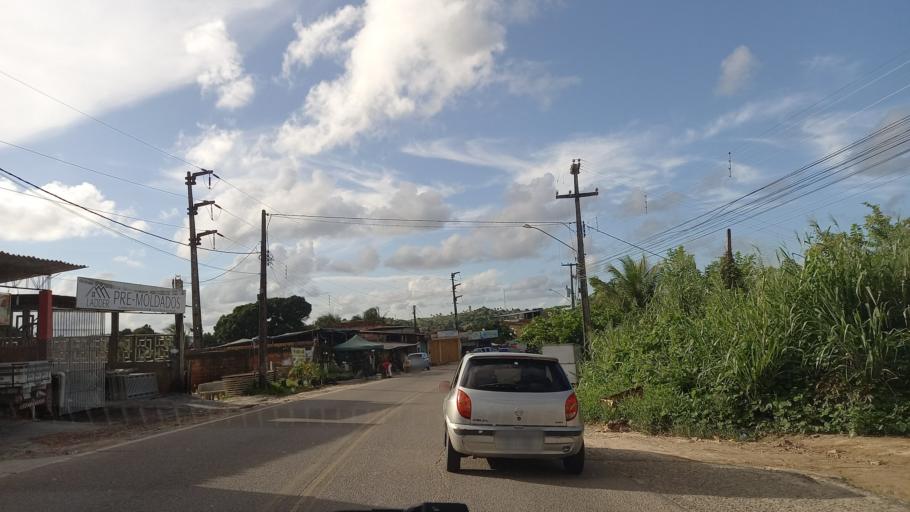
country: BR
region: Pernambuco
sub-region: Rio Formoso
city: Rio Formoso
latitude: -8.6692
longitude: -35.1582
